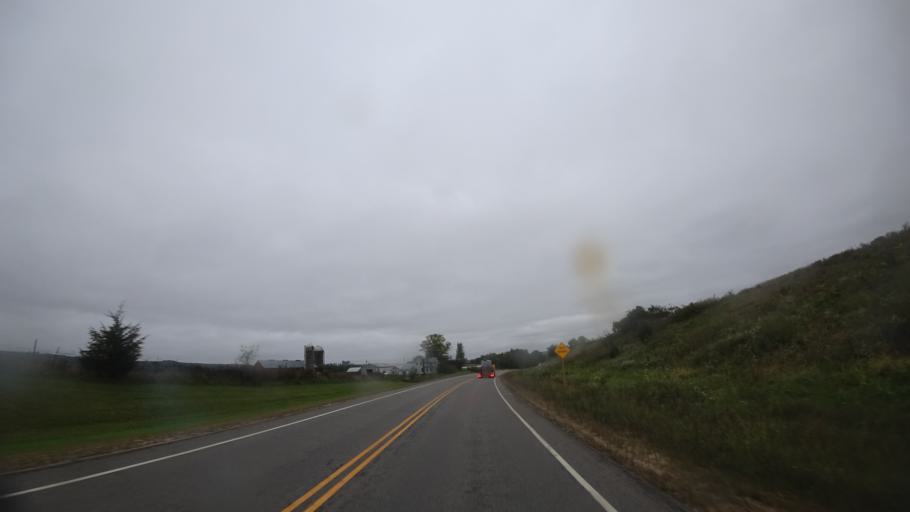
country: US
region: Wisconsin
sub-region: Crawford County
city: Prairie du Chien
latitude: 43.0280
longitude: -91.0176
